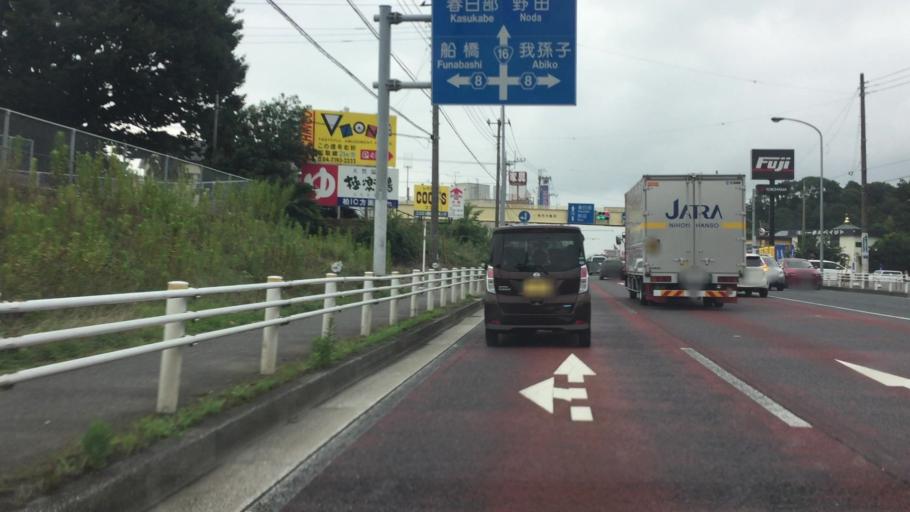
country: JP
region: Chiba
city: Abiko
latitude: 35.8364
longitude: 140.0070
